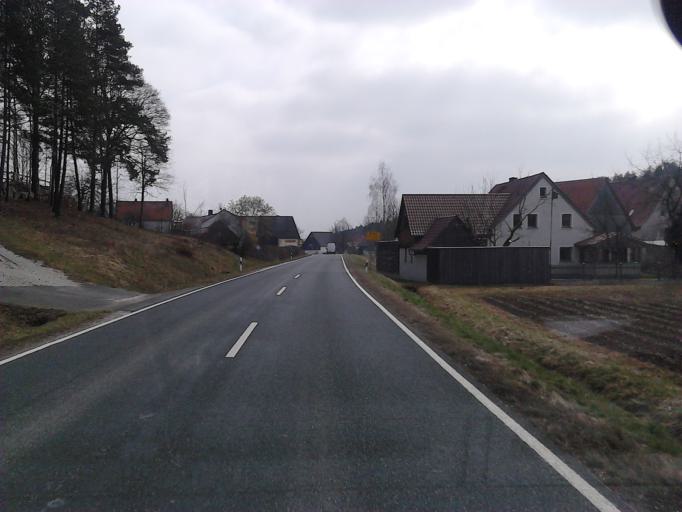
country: DE
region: Bavaria
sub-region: Regierungsbezirk Mittelfranken
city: Velden
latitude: 49.6433
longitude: 11.5077
